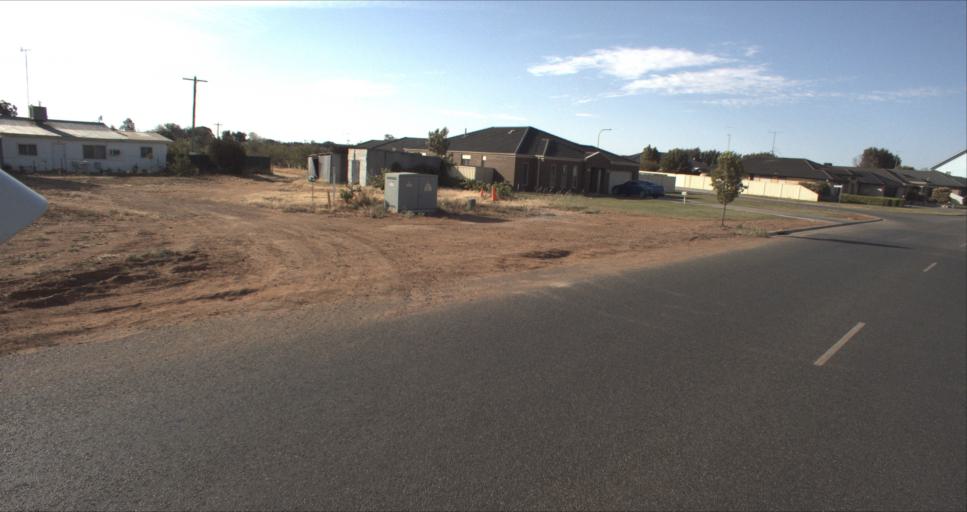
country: AU
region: New South Wales
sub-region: Leeton
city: Leeton
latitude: -34.5419
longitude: 146.4002
